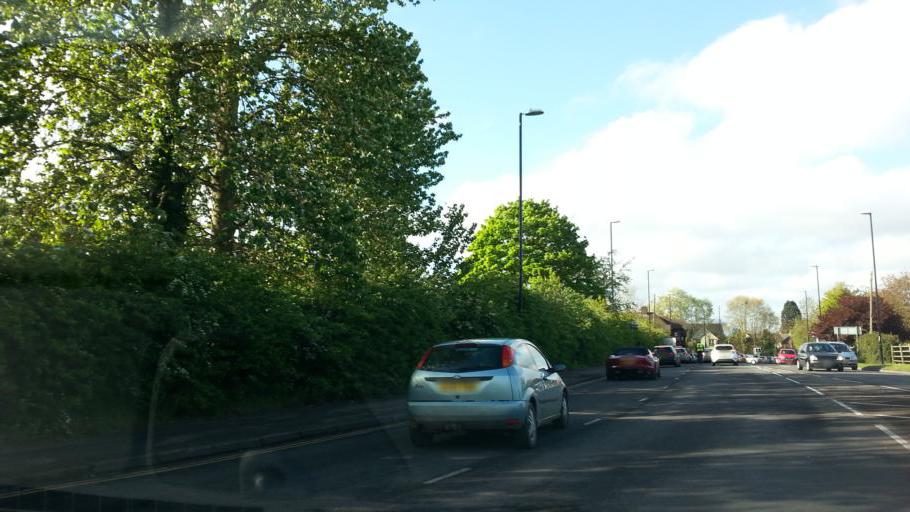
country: GB
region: England
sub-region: Warwickshire
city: Ryton on Dunsmore
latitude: 52.4040
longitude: -1.4450
